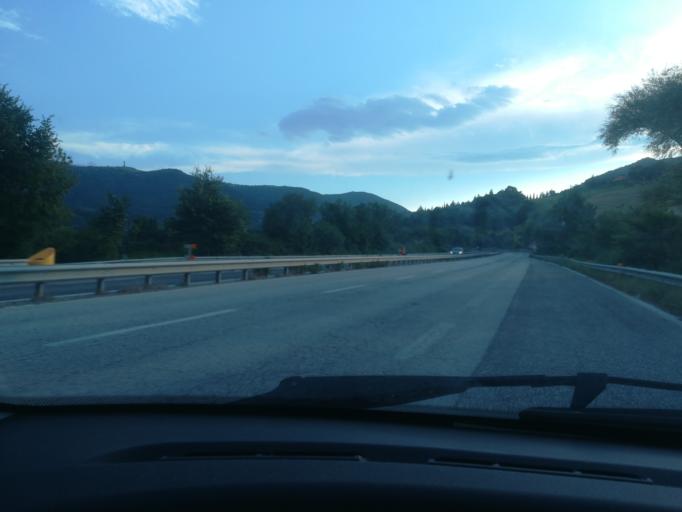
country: IT
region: The Marches
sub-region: Provincia di Macerata
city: Caldarola
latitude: 43.1510
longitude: 13.2165
